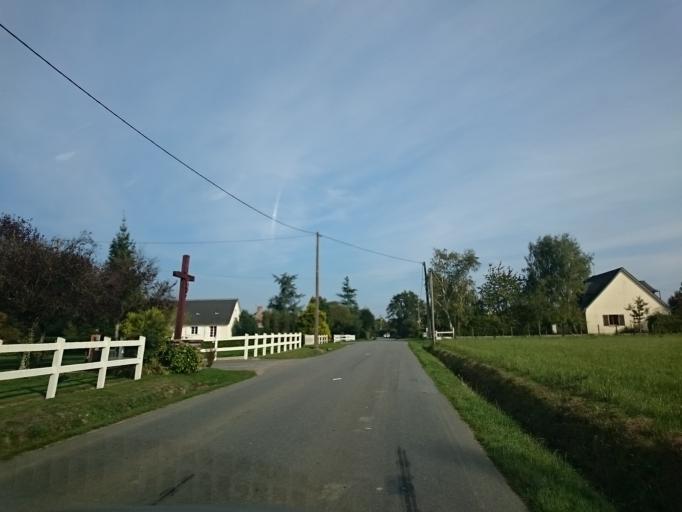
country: FR
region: Brittany
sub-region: Departement d'Ille-et-Vilaine
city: Corps-Nuds
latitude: 47.9513
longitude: -1.5482
